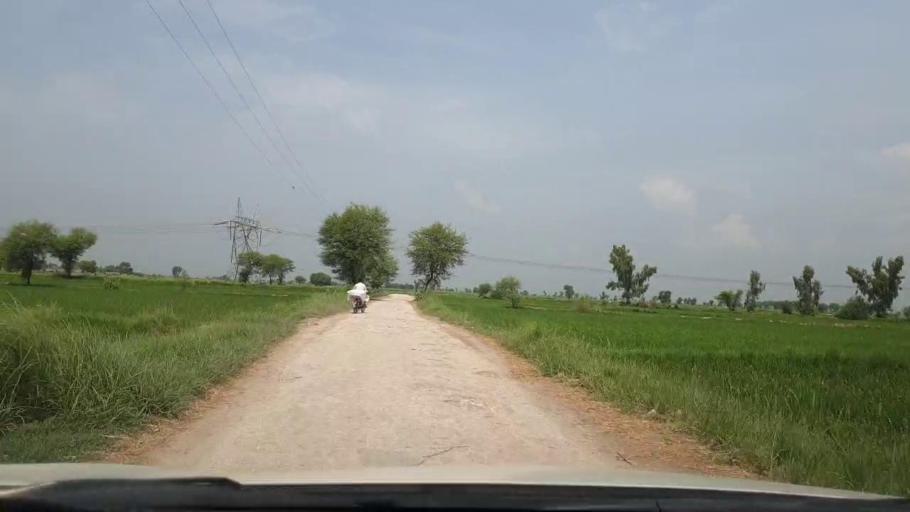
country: PK
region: Sindh
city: Dokri
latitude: 27.3896
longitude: 68.0563
